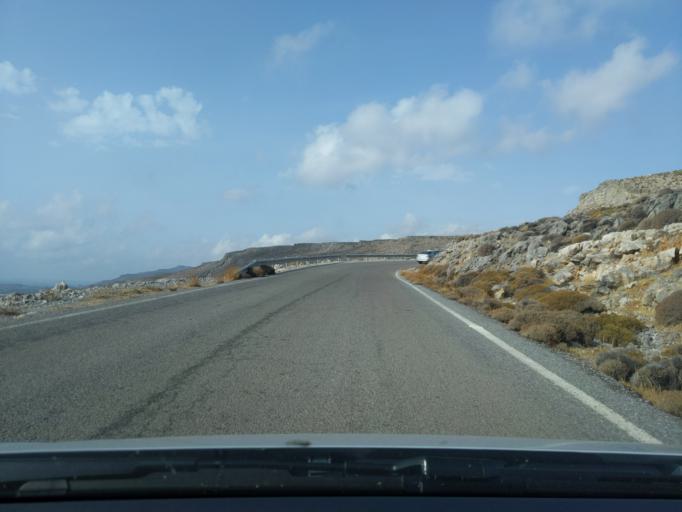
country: GR
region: Crete
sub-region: Nomos Lasithiou
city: Palekastro
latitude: 35.0846
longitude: 26.2624
